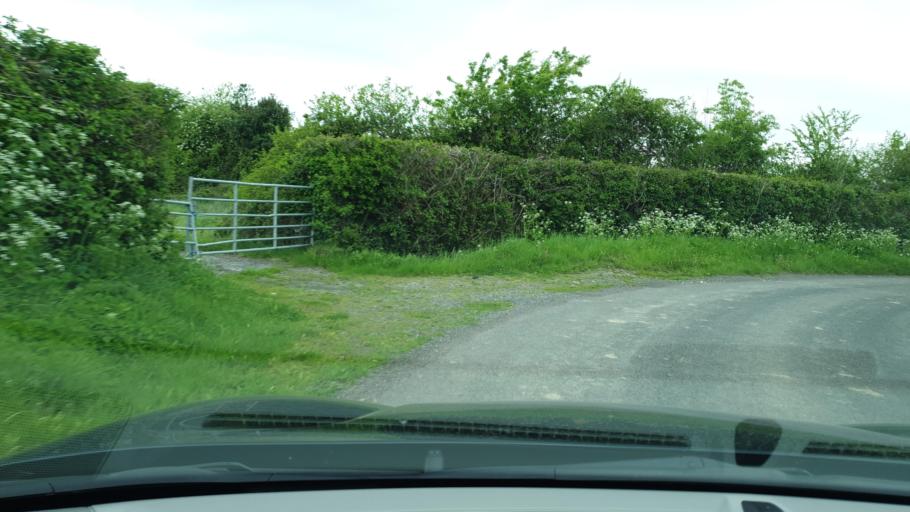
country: IE
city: Confey
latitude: 53.4258
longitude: -6.5335
